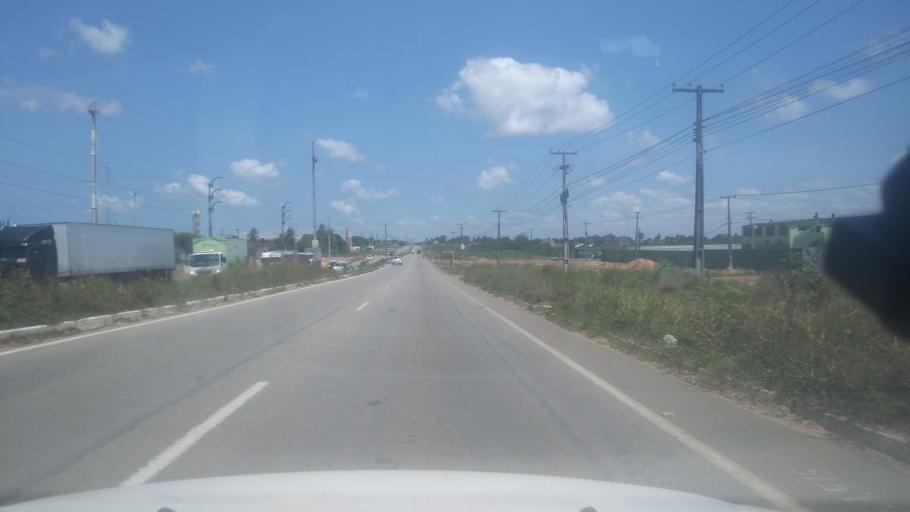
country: BR
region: Rio Grande do Norte
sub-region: Extremoz
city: Extremoz
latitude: -5.7414
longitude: -35.2903
